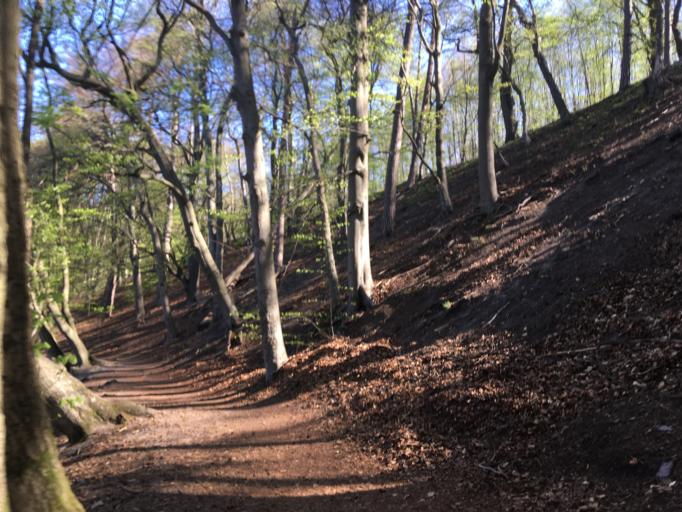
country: DE
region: Brandenburg
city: Wandlitz
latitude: 52.7505
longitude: 13.5299
